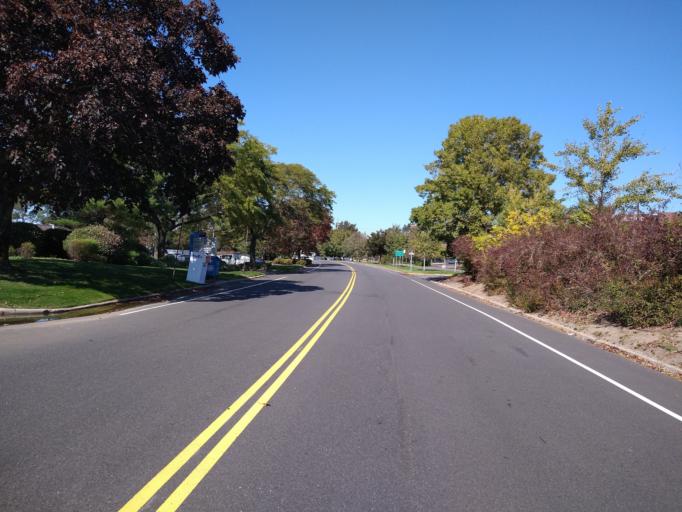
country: US
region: New York
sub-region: Nassau County
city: Woodbury
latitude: 40.8040
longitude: -73.4775
